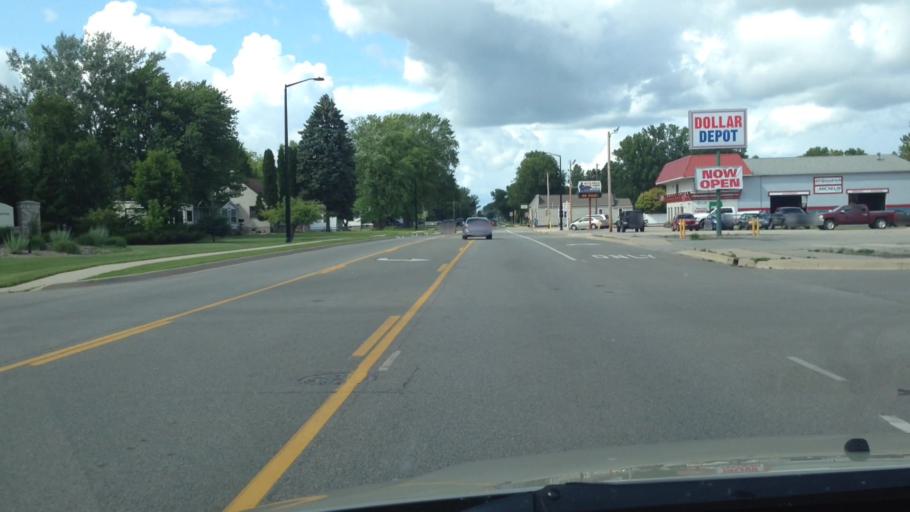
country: US
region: Michigan
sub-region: Menominee County
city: Menominee
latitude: 45.1367
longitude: -87.6124
